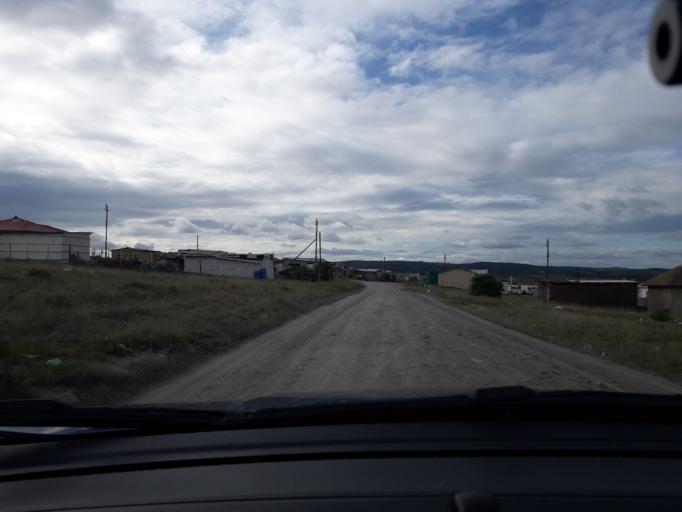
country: ZA
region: Eastern Cape
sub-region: Buffalo City Metropolitan Municipality
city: East London
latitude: -32.8530
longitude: 27.9842
